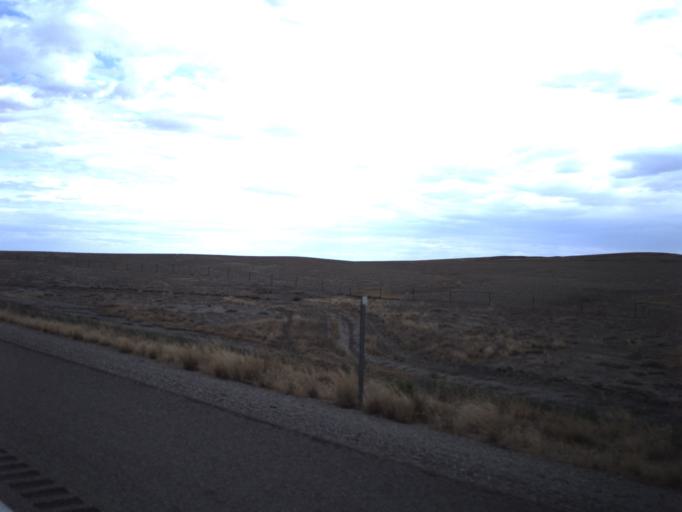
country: US
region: Utah
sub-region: Grand County
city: Moab
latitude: 38.9555
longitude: -110.0568
